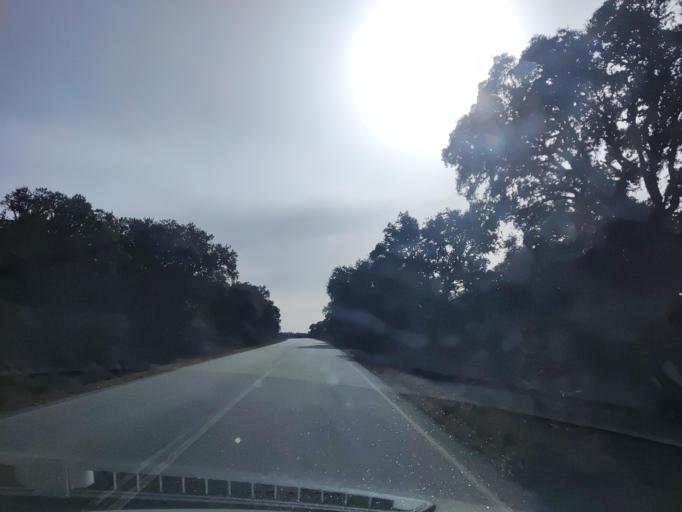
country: ES
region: Castille and Leon
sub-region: Provincia de Salamanca
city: Aldea del Obispo
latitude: 40.6836
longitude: -6.7962
